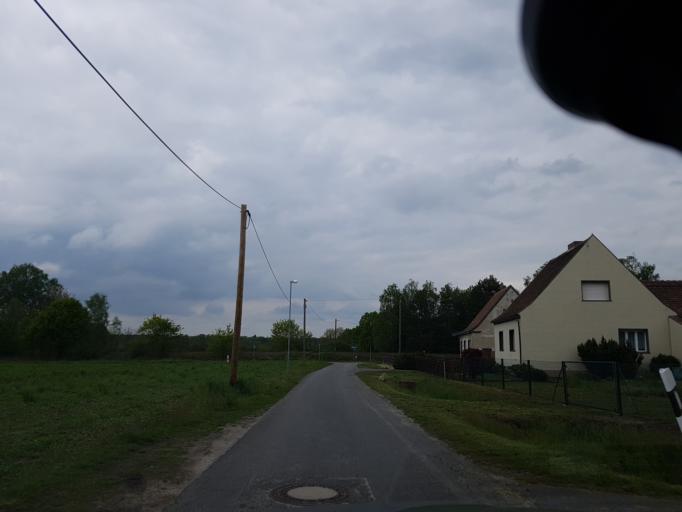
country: DE
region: Brandenburg
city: Crinitz
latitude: 51.7403
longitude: 13.7633
